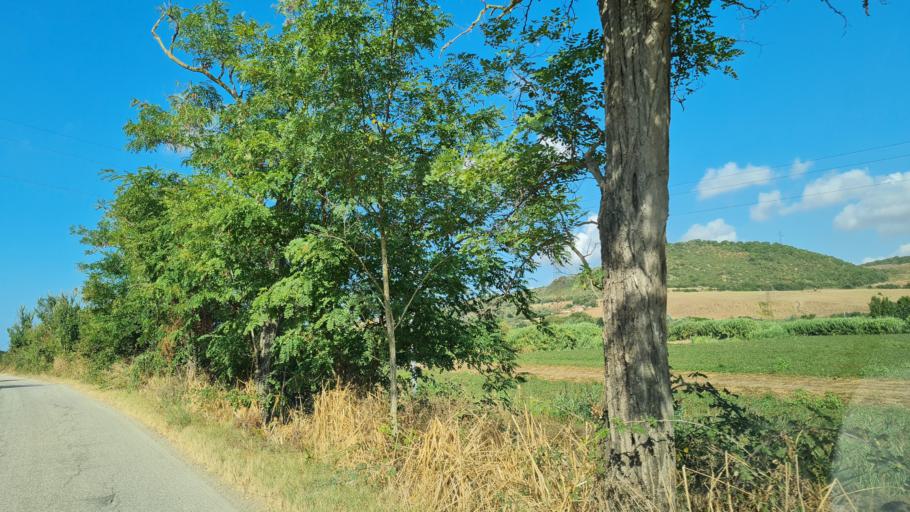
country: IT
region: Latium
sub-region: Provincia di Viterbo
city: Tarquinia
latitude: 42.2612
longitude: 11.7563
